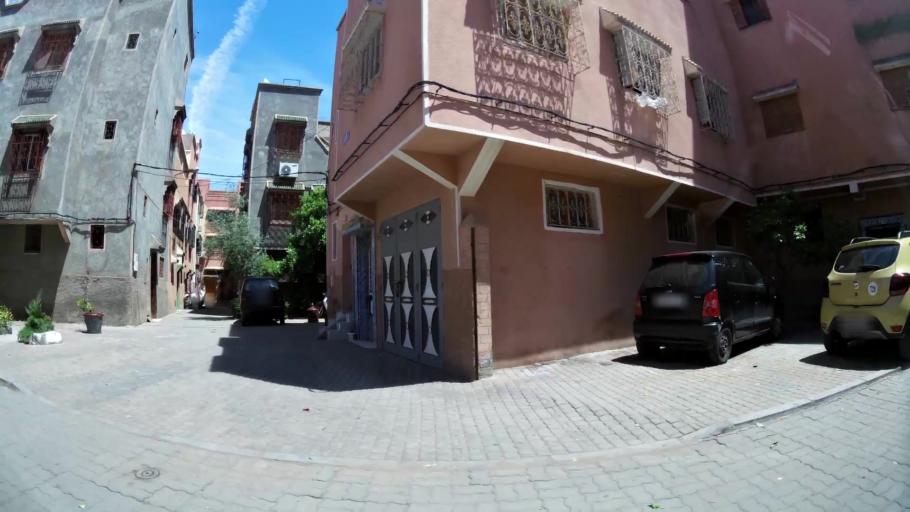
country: MA
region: Marrakech-Tensift-Al Haouz
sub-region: Marrakech
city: Marrakesh
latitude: 31.6384
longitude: -8.0451
